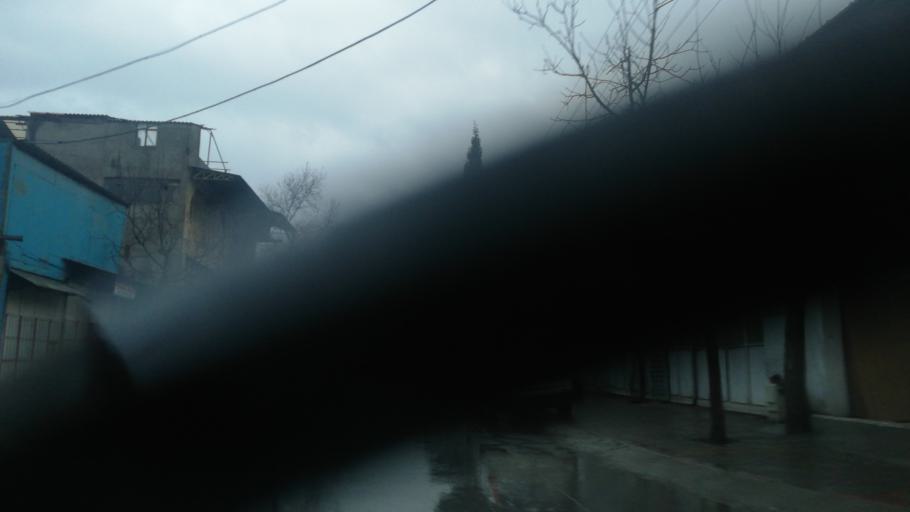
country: TR
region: Kahramanmaras
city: Kahramanmaras
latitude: 37.5613
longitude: 36.9596
